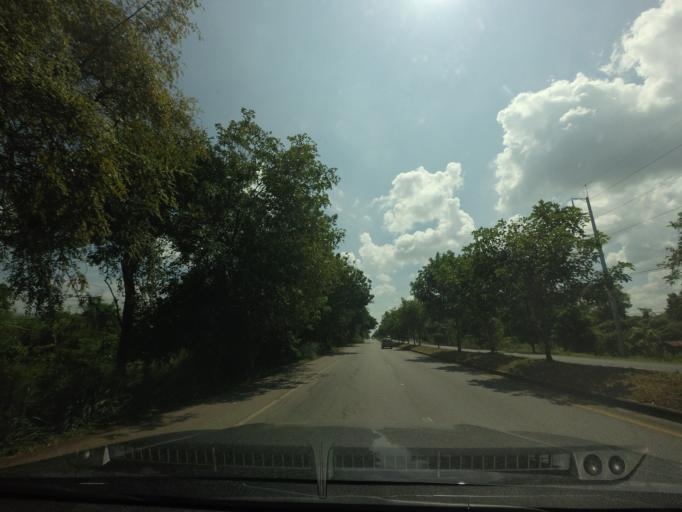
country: TH
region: Phetchabun
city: Nong Phai
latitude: 16.0378
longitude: 101.0785
